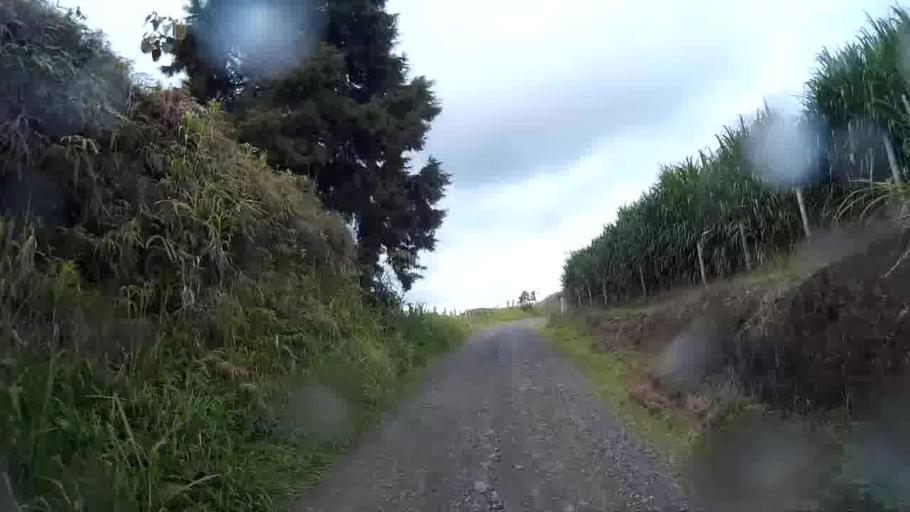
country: CO
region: Quindio
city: Filandia
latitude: 4.7006
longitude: -75.6718
